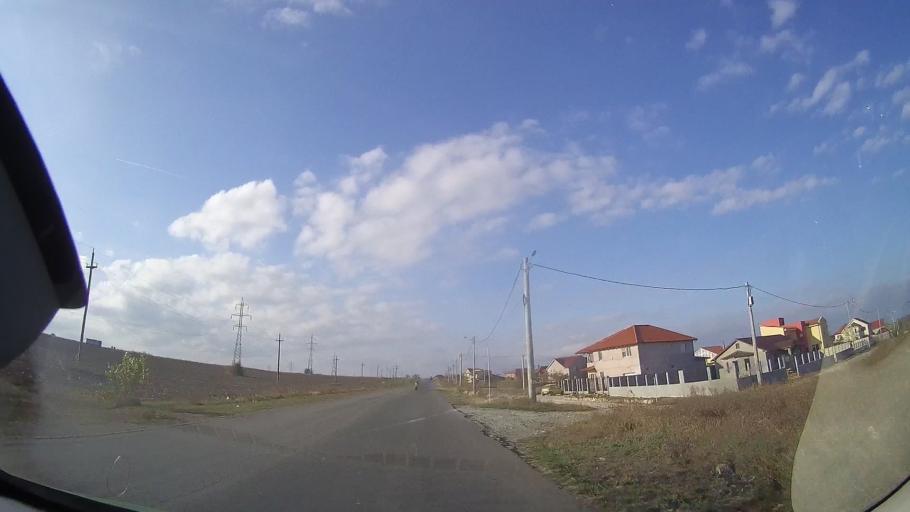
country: RO
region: Constanta
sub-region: Comuna Limanu
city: Limanu
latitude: 43.7910
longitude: 28.5487
